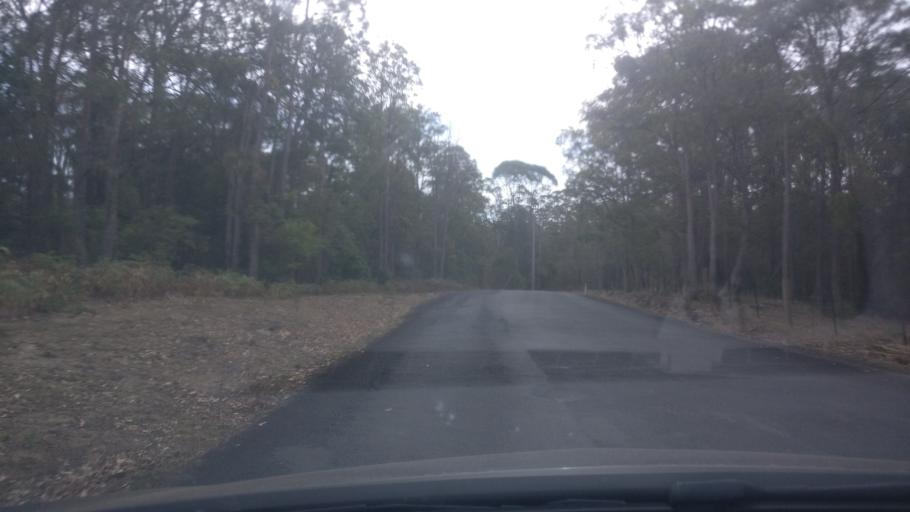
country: AU
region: New South Wales
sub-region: Shoalhaven Shire
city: Kangaroo Valley
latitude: -34.7223
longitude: 150.4749
